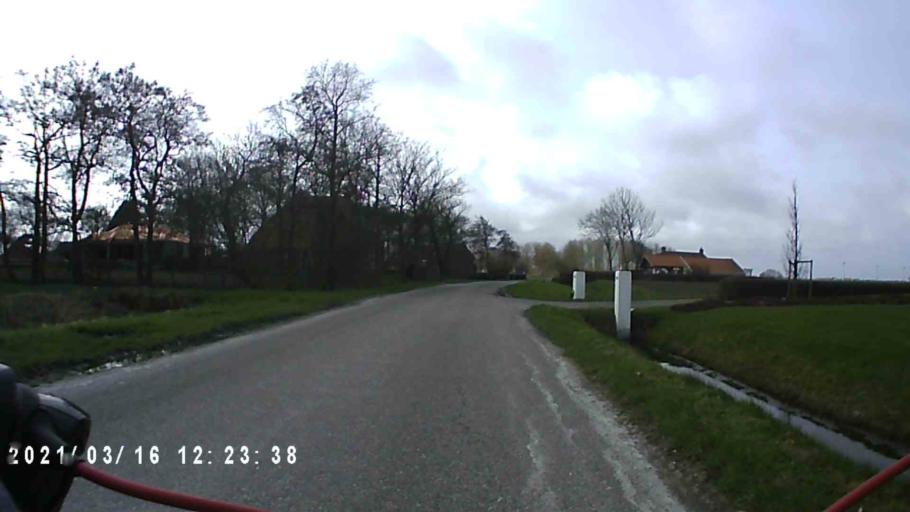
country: NL
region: Friesland
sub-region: Gemeente Ferwerderadiel
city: Hallum
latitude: 53.3021
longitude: 5.7543
